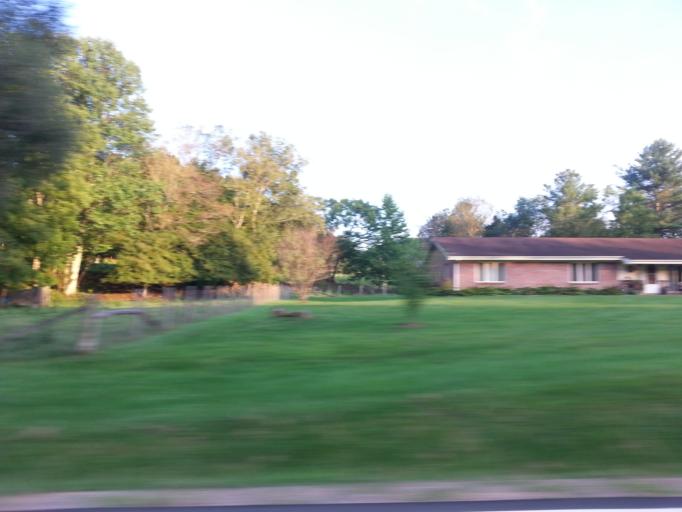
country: US
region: Tennessee
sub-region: Johnson County
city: Mountain City
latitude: 36.5593
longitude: -81.8839
